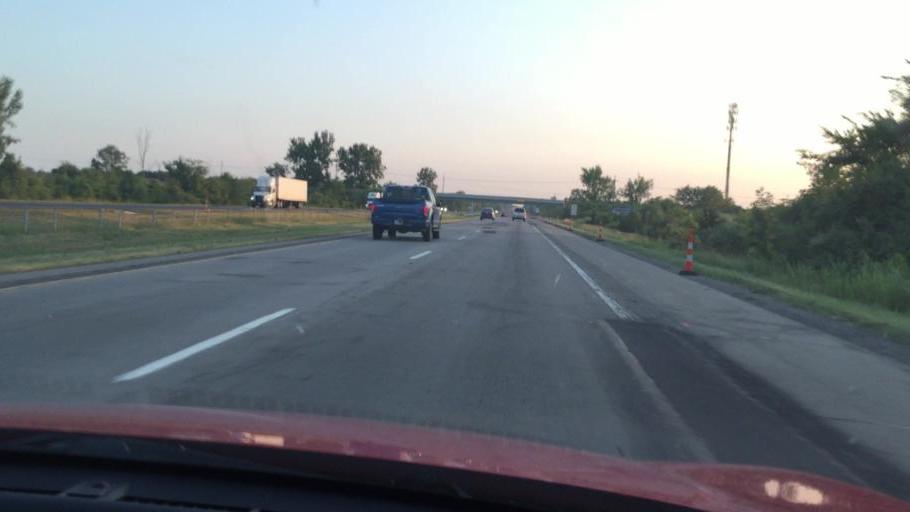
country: US
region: Michigan
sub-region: Washtenaw County
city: Milan
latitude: 42.1104
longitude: -83.6822
